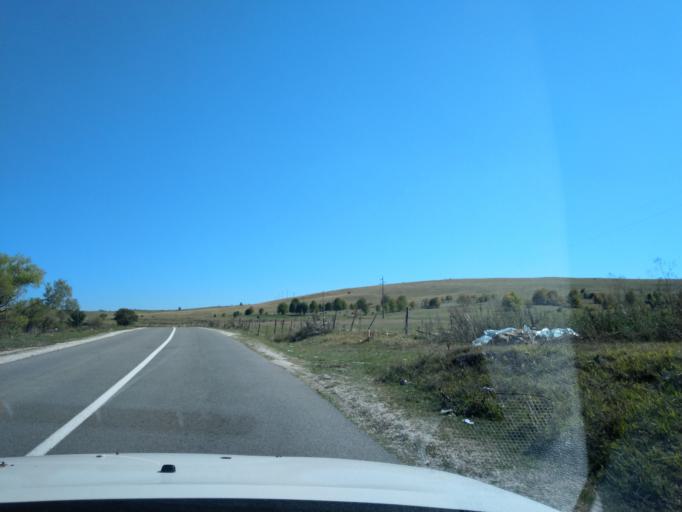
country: RS
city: Sokolovica
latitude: 43.2743
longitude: 20.2013
